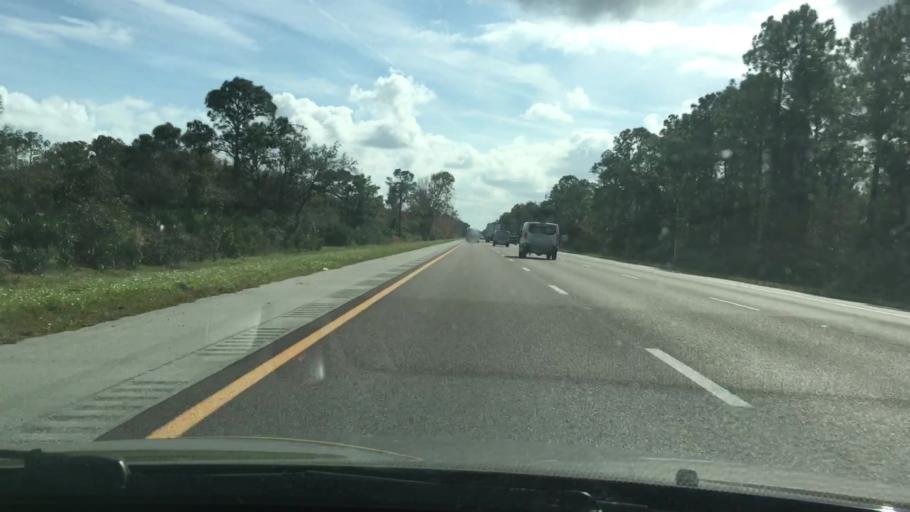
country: US
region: Florida
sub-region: Volusia County
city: Oak Hill
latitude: 28.8898
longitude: -80.9272
